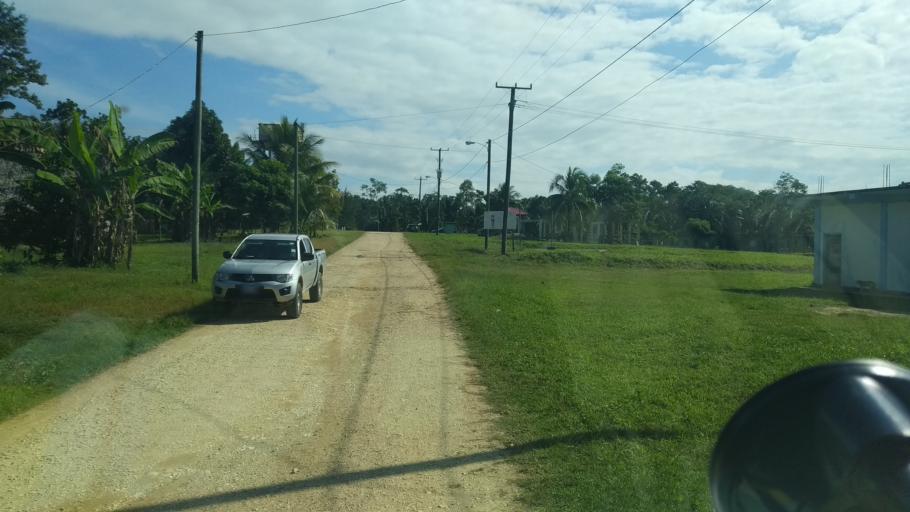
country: BZ
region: Toledo
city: Punta Gorda
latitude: 16.2162
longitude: -88.9052
